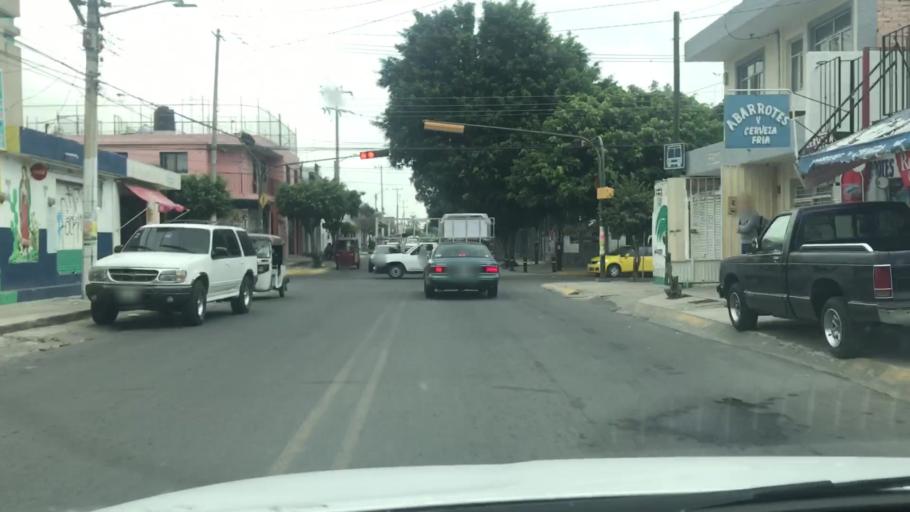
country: MX
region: Jalisco
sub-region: Tlajomulco de Zuniga
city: Palomar
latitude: 20.6404
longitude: -103.4528
